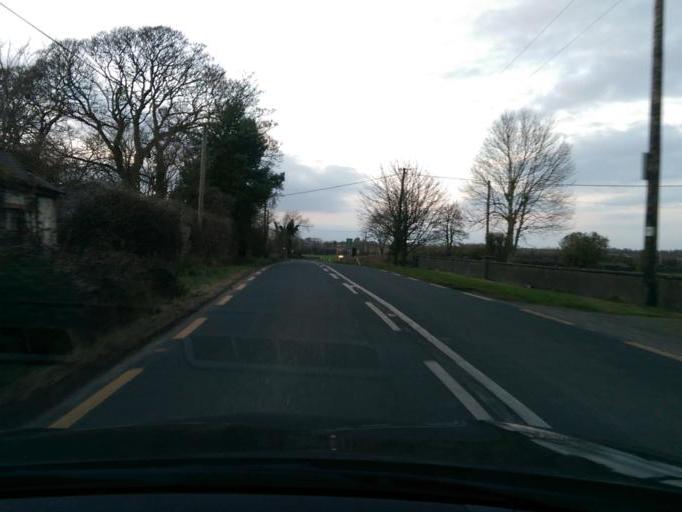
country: IE
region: Connaught
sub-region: County Galway
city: Portumna
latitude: 53.0046
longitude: -8.1251
